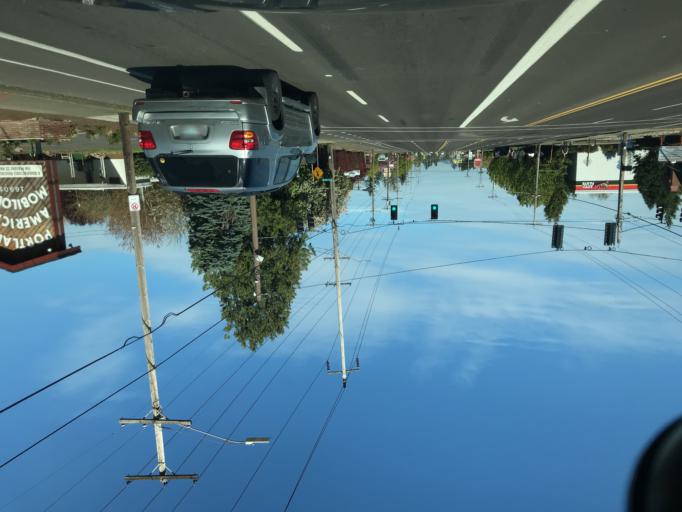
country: US
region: Oregon
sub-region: Multnomah County
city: Gresham
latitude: 45.5046
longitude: -122.4891
